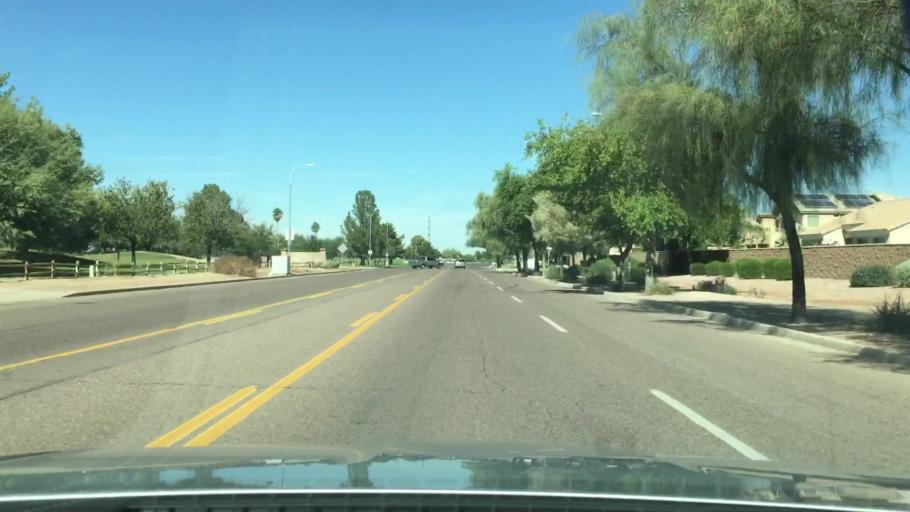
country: US
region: Arizona
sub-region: Maricopa County
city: Laveen
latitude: 33.3714
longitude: -112.1347
